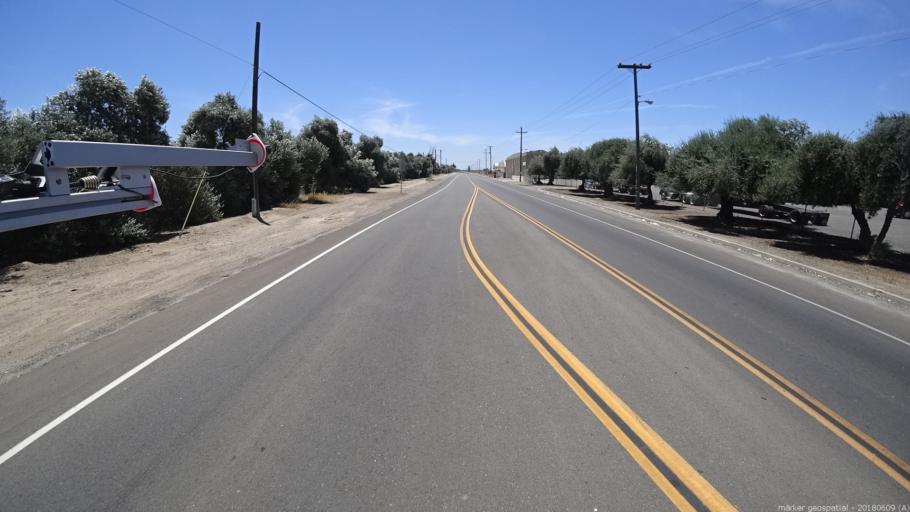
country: US
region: California
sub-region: Madera County
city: Madera
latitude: 36.9377
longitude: -120.0741
